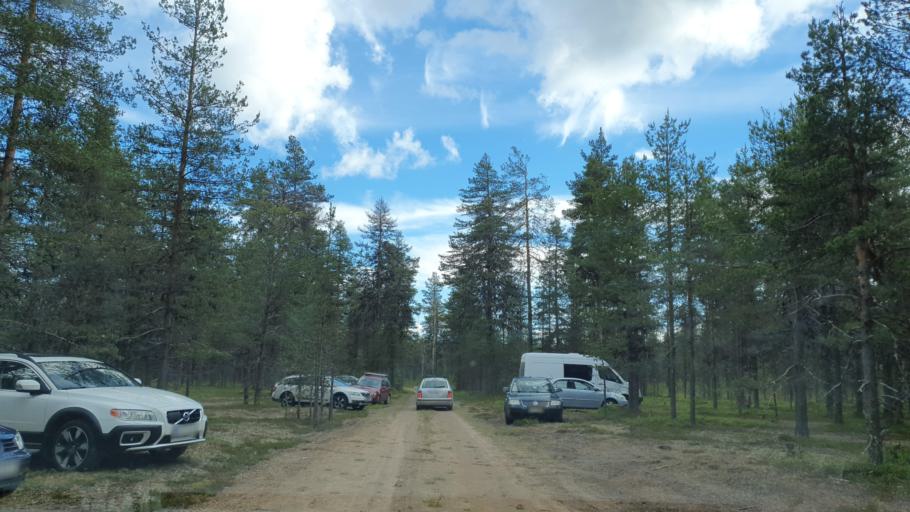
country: FI
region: Lapland
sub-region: Tunturi-Lappi
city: Kolari
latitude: 67.5396
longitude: 23.9133
